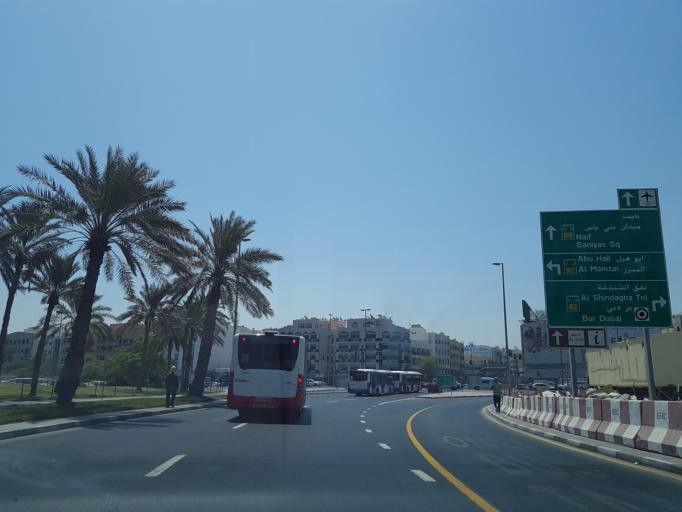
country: AE
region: Ash Shariqah
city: Sharjah
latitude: 25.2775
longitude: 55.3041
